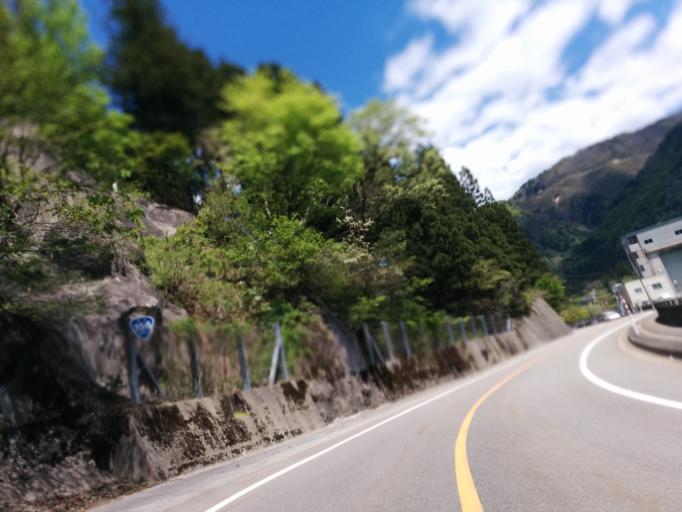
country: JP
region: Toyama
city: Fukumitsu
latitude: 36.3757
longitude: 136.8688
